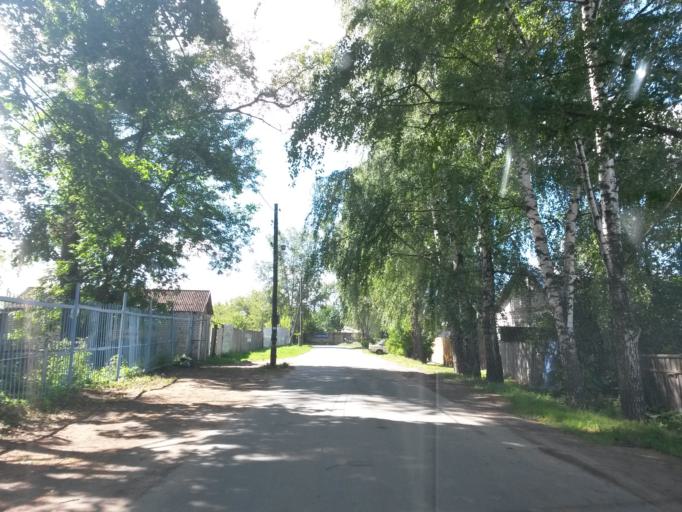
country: RU
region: Jaroslavl
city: Yaroslavl
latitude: 57.6040
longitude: 39.8905
